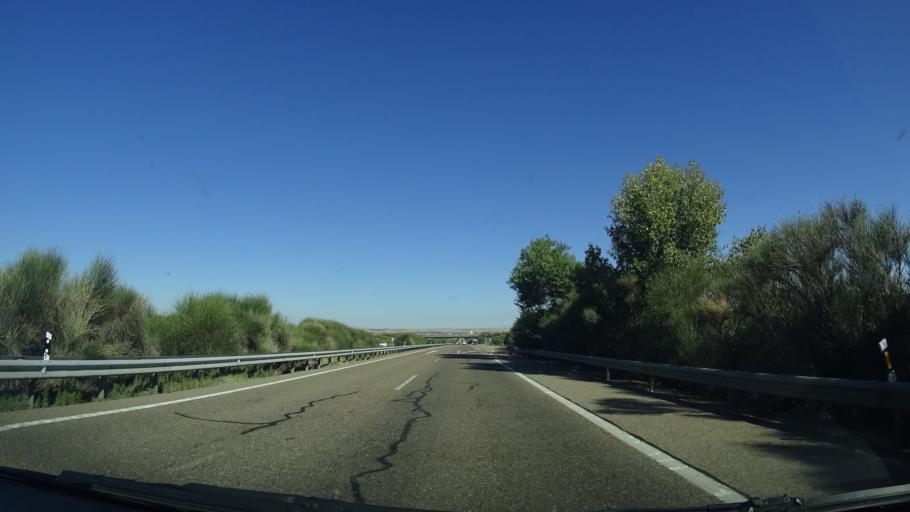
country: ES
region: Castille and Leon
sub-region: Provincia de Zamora
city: Quintanilla del Monte
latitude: 41.8243
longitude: -5.3741
